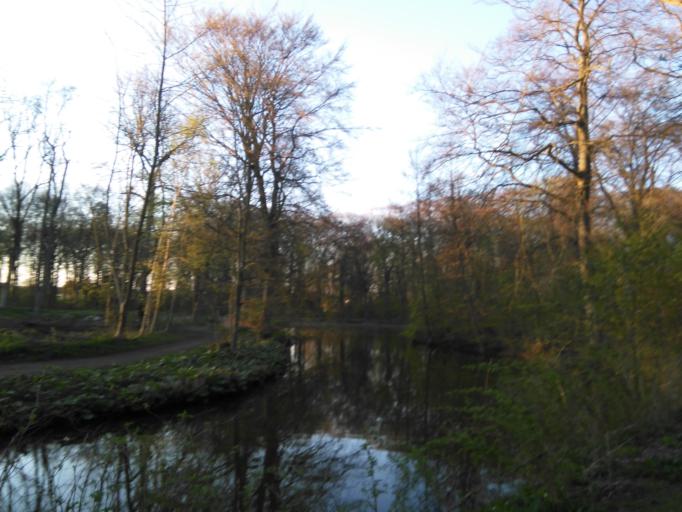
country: DK
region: Central Jutland
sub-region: Arhus Kommune
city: Arhus
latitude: 56.1349
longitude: 10.1934
